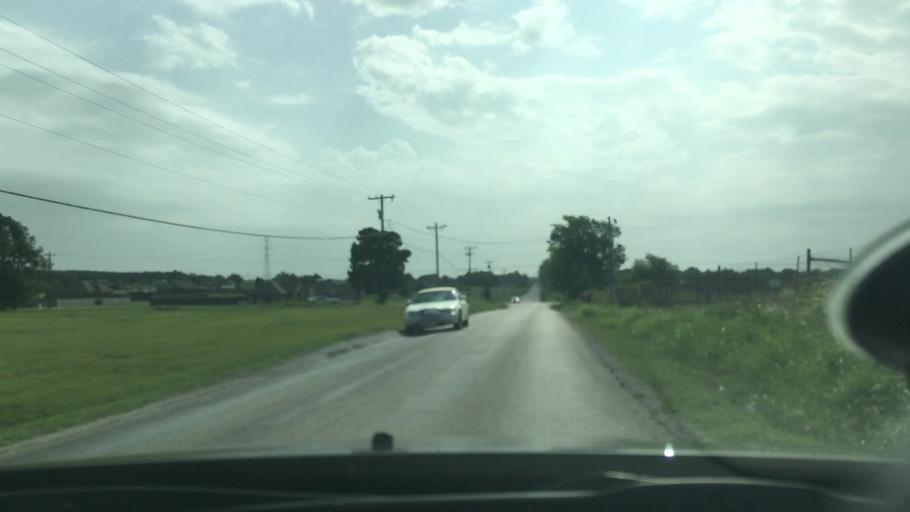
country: US
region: Oklahoma
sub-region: Carter County
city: Lone Grove
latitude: 34.2020
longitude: -97.2492
